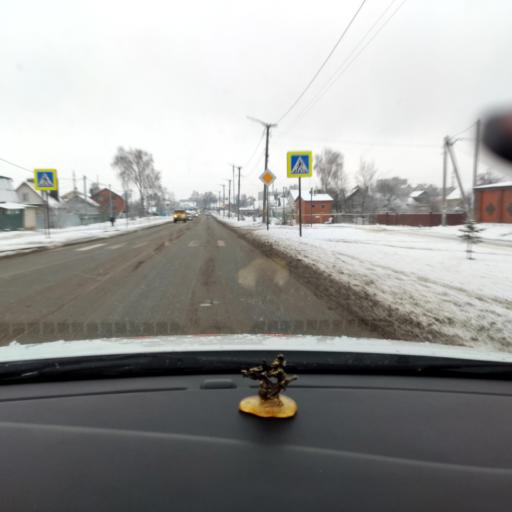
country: RU
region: Tatarstan
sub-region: Zelenodol'skiy Rayon
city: Zelenodolsk
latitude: 55.8550
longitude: 48.5307
